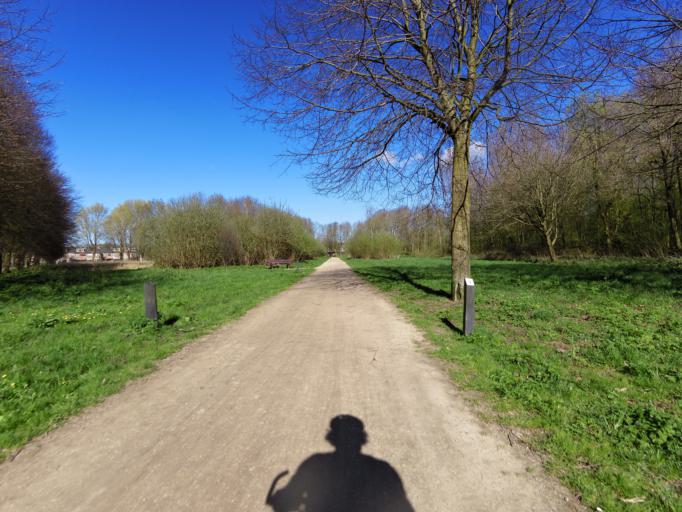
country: NL
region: South Holland
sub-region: Gemeente Waddinxveen
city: Groenswaard
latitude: 52.0627
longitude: 4.6442
